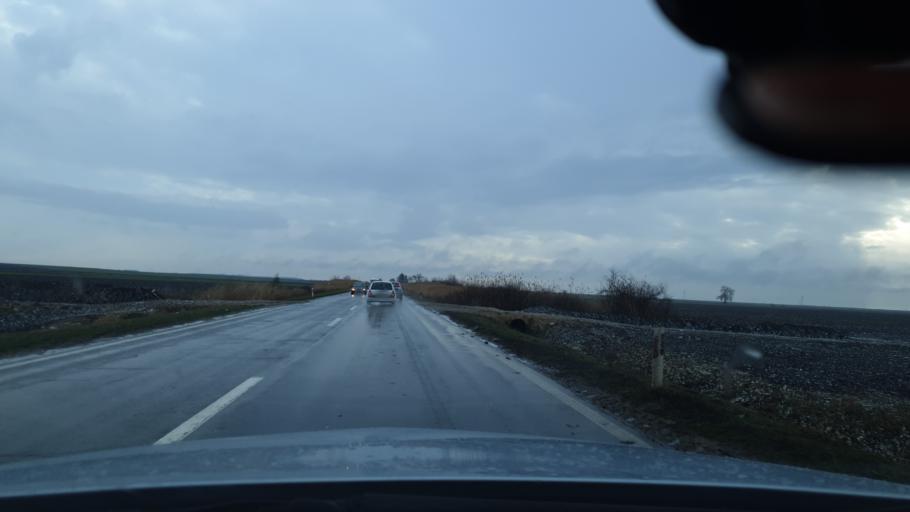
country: RS
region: Autonomna Pokrajina Vojvodina
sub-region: Juznobanatski Okrug
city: Pancevo
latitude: 44.8357
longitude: 20.8148
